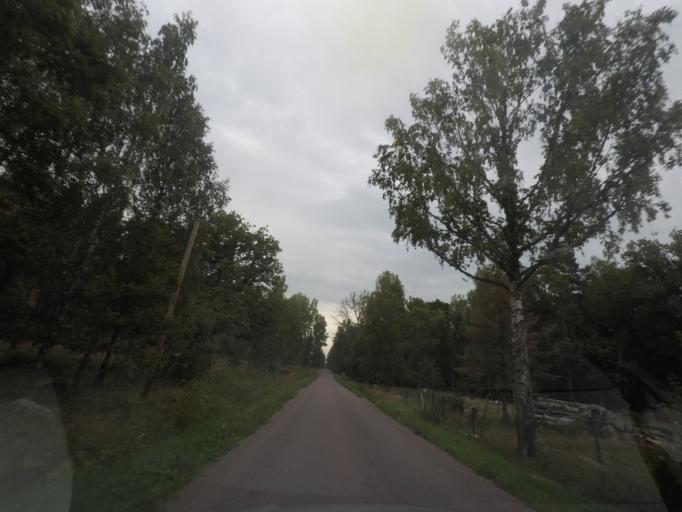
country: SE
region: Vaestmanland
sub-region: Hallstahammars Kommun
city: Kolback
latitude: 59.4924
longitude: 16.1928
